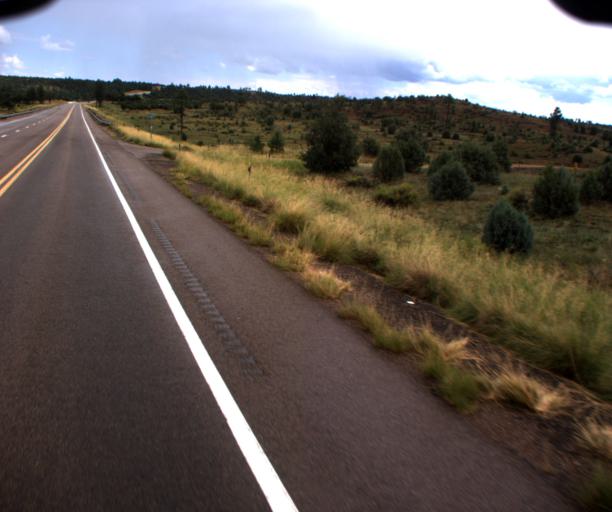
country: US
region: Arizona
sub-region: Navajo County
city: Heber-Overgaard
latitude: 34.3656
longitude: -110.4141
